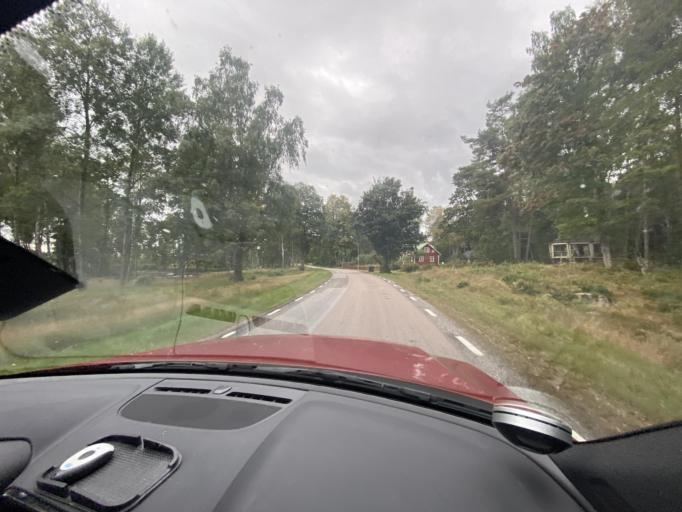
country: SE
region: Kronoberg
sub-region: Markaryds Kommun
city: Markaryd
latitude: 56.5034
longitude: 13.5496
